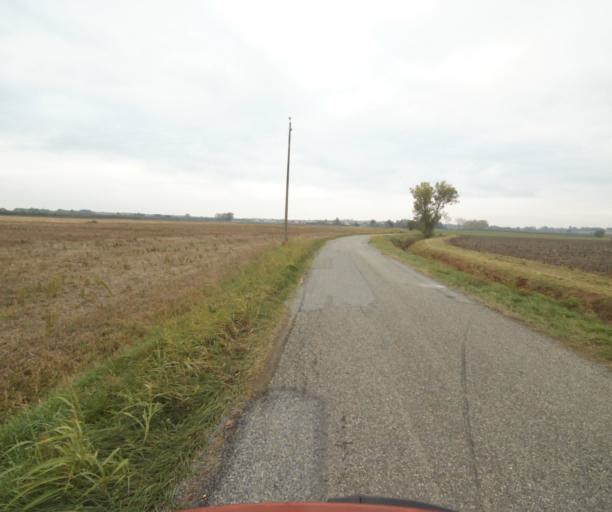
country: FR
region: Midi-Pyrenees
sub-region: Departement du Tarn-et-Garonne
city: Verdun-sur-Garonne
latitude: 43.8171
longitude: 1.2237
